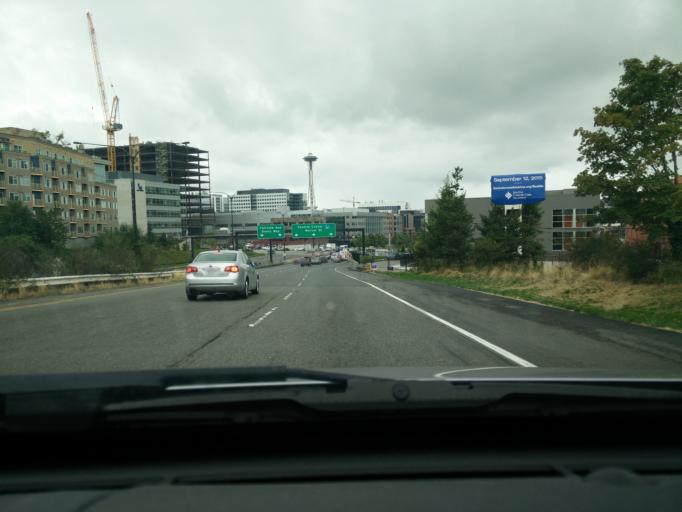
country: US
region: Washington
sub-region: King County
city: Seattle
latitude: 47.6254
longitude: -122.3316
